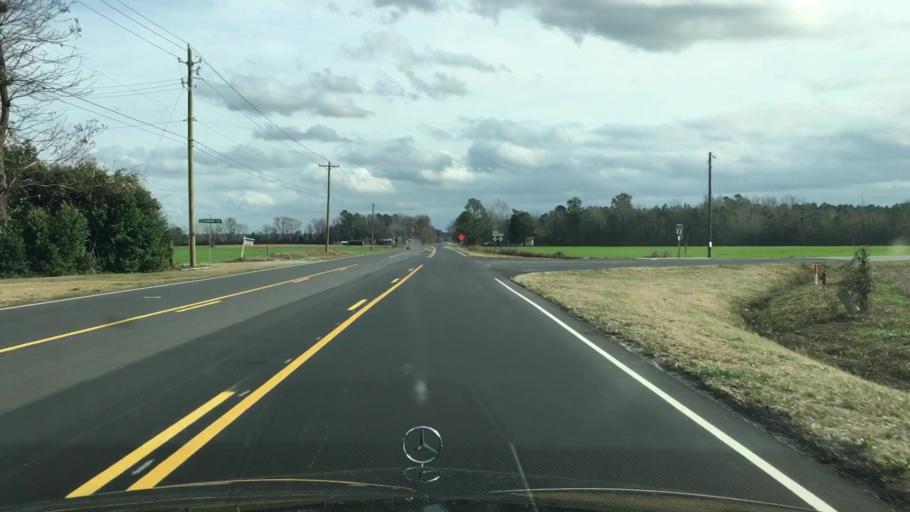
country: US
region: North Carolina
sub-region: Duplin County
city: Warsaw
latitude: 34.9840
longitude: -78.0397
